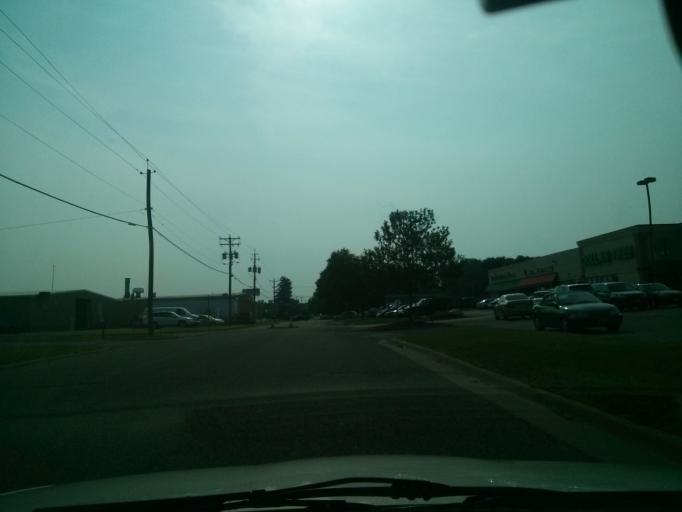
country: US
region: Wisconsin
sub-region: Saint Croix County
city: Hudson
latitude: 44.9642
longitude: -92.7335
